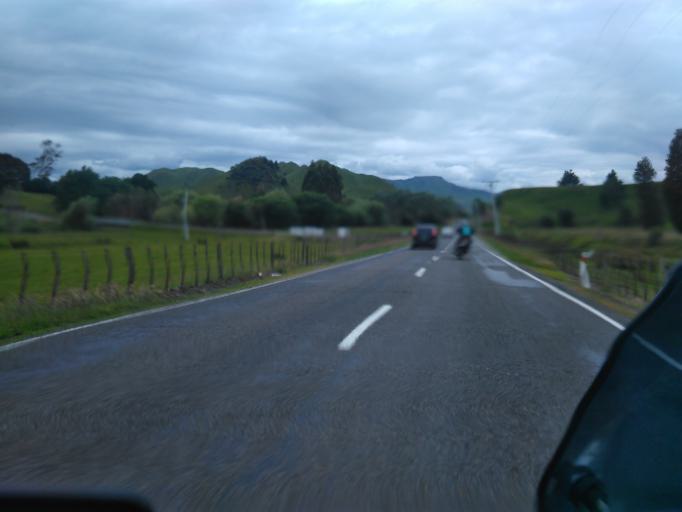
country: NZ
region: Bay of Plenty
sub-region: Opotiki District
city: Opotiki
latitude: -38.3626
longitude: 177.4967
